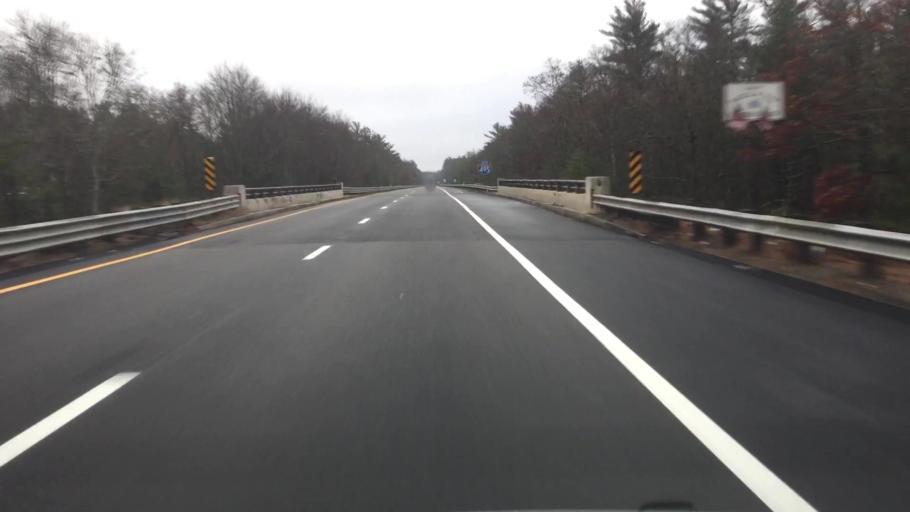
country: US
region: Massachusetts
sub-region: Plymouth County
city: West Wareham
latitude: 41.8248
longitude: -70.8091
